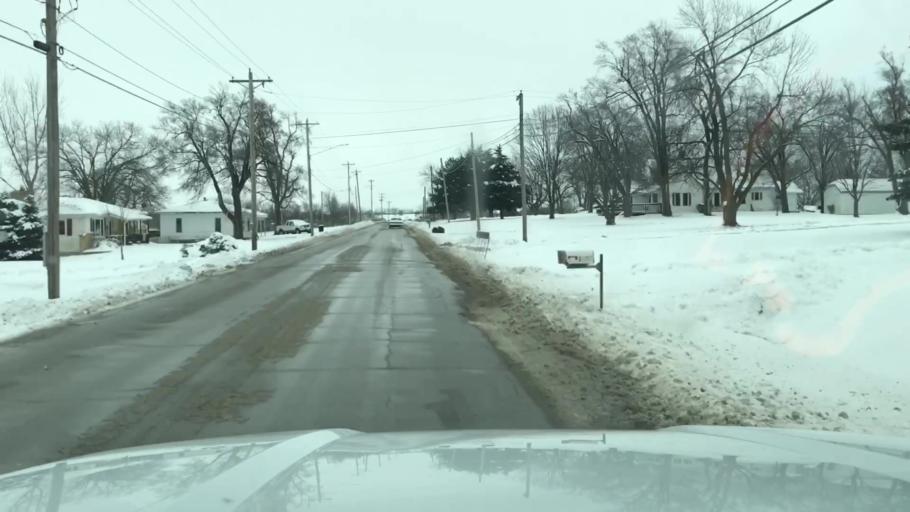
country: US
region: Missouri
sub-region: Clinton County
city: Cameron
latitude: 39.7424
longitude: -94.2232
